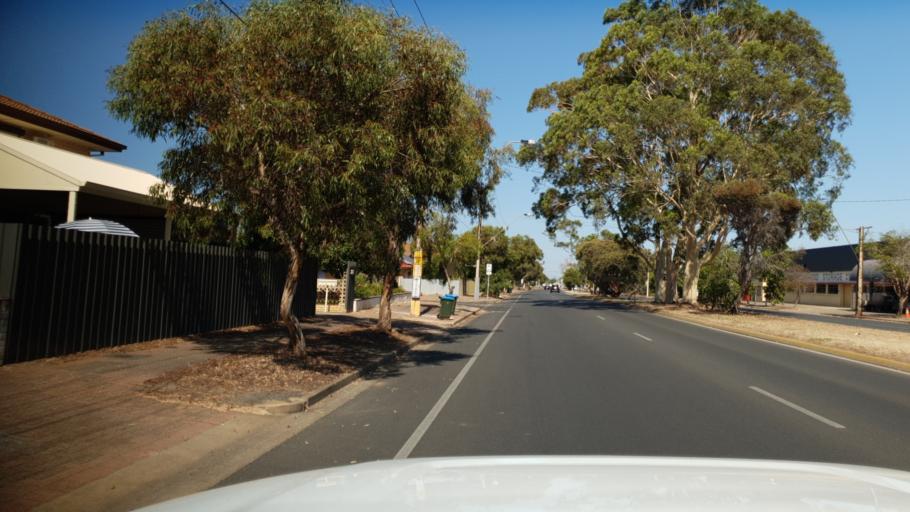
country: AU
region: South Australia
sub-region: Marion
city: Clovelly Park
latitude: -34.9927
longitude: 138.5817
